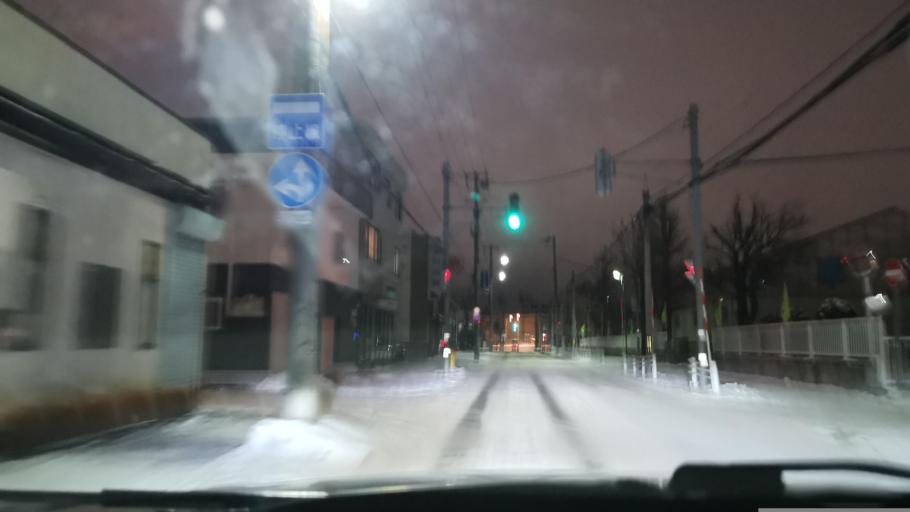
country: JP
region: Hokkaido
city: Sapporo
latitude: 43.0620
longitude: 141.3817
